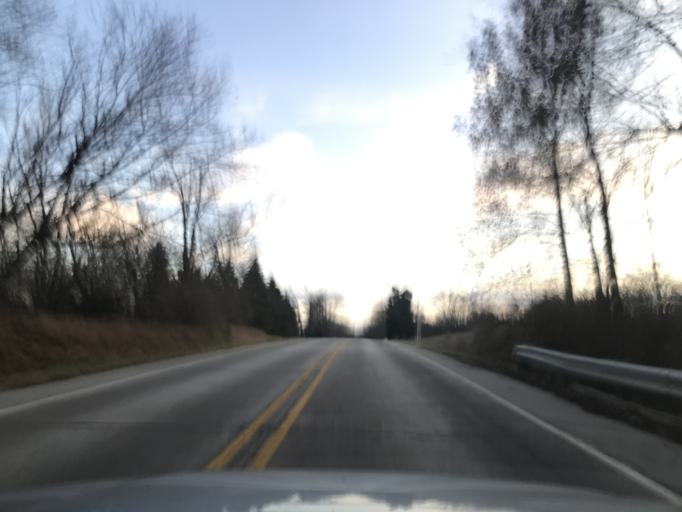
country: US
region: Illinois
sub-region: Henderson County
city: Oquawka
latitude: 40.8997
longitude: -90.8645
